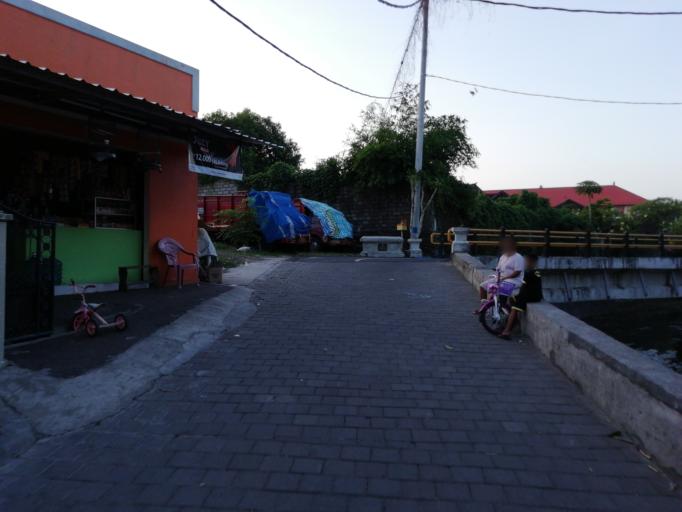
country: ID
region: Bali
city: Denpasar
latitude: -8.6405
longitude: 115.2134
